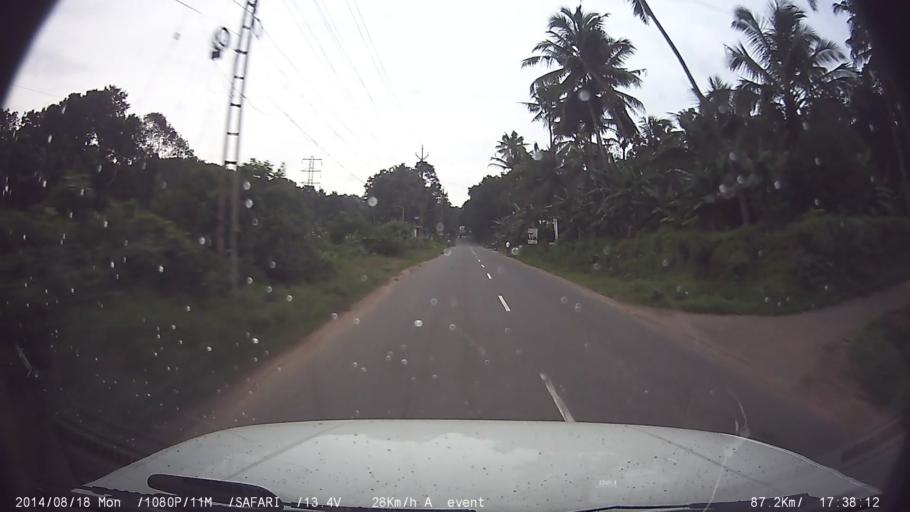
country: IN
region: Kerala
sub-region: Ernakulam
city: Muvattupuzha
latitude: 9.9143
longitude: 76.5832
